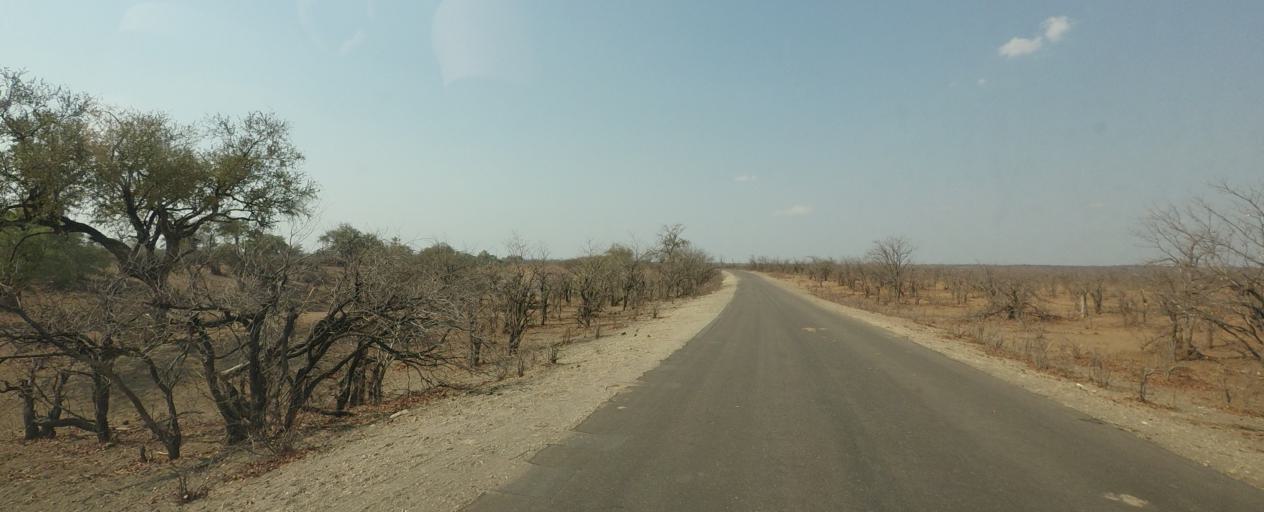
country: ZA
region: Limpopo
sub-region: Mopani District Municipality
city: Giyani
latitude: -23.1389
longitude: 31.3752
